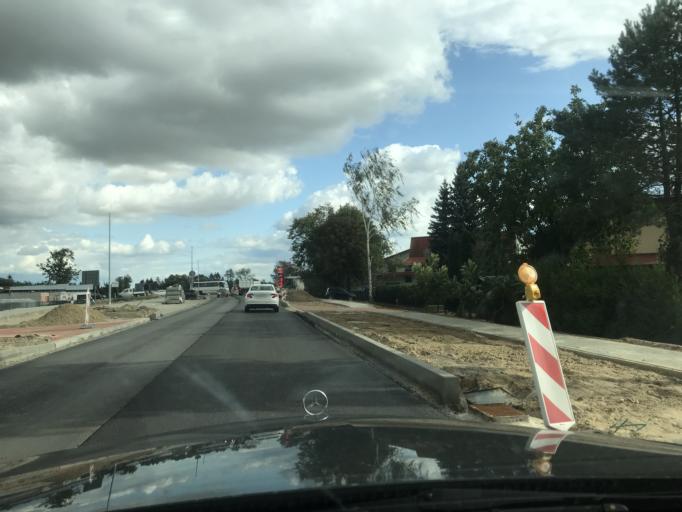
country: PL
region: Lublin Voivodeship
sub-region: Powiat lubartowski
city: Lubartow
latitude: 51.4750
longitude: 22.6028
